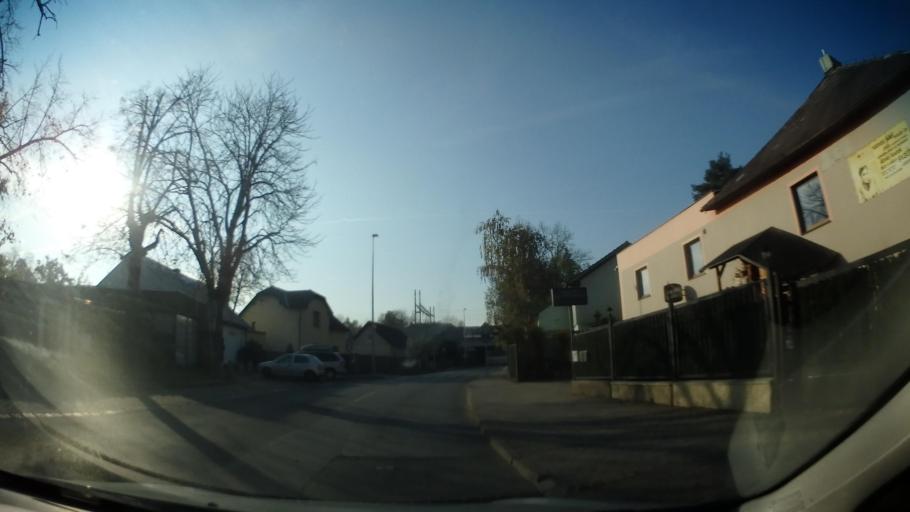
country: CZ
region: Praha
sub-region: Praha 14
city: Dolni Pocernice
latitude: 50.0875
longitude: 14.5767
